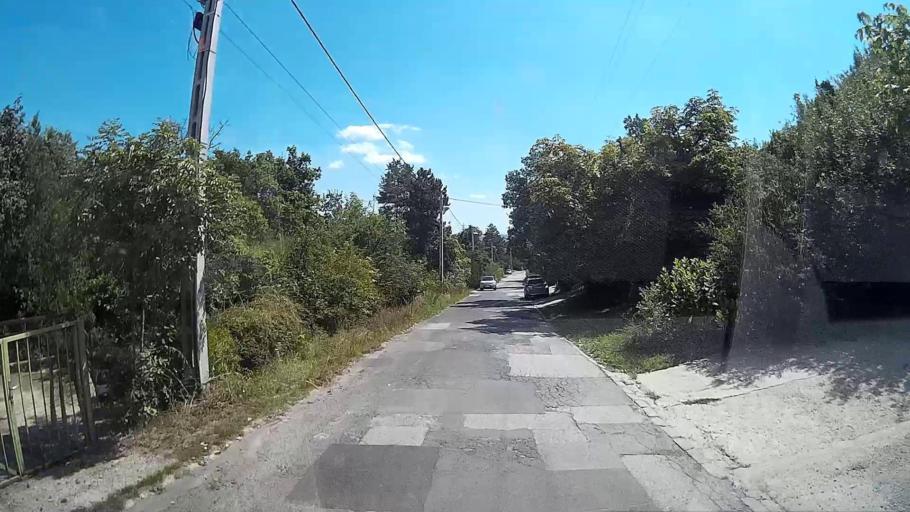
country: HU
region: Pest
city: Leanyfalu
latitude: 47.6964
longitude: 19.0806
